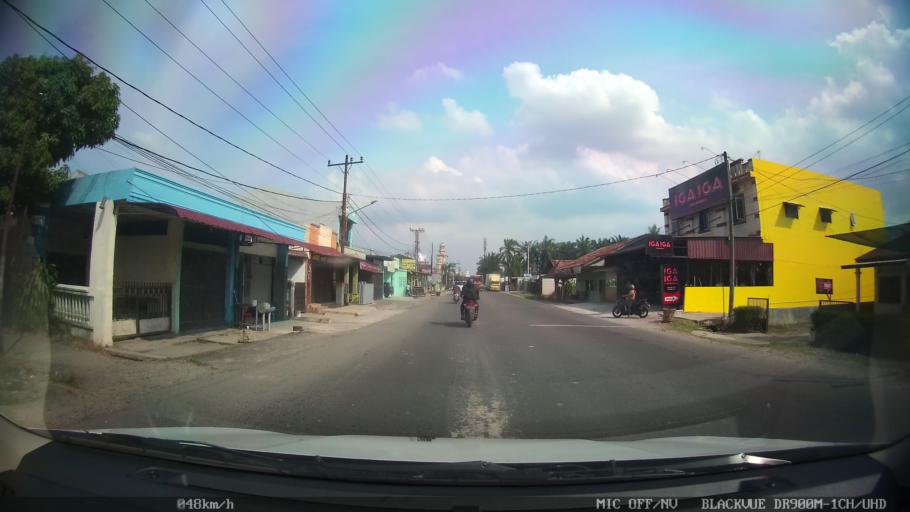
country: ID
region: North Sumatra
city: Binjai
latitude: 3.6291
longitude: 98.4929
